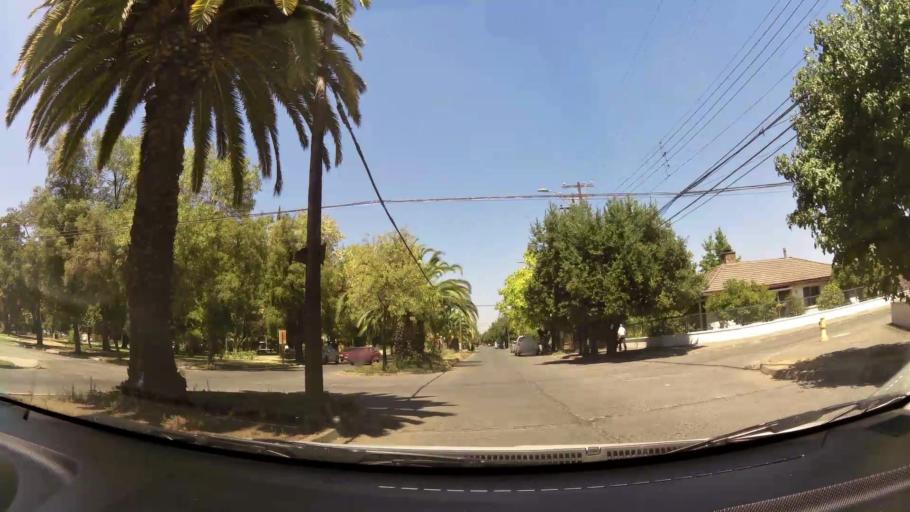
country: CL
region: Maule
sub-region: Provincia de Curico
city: Curico
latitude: -34.9868
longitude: -71.2288
